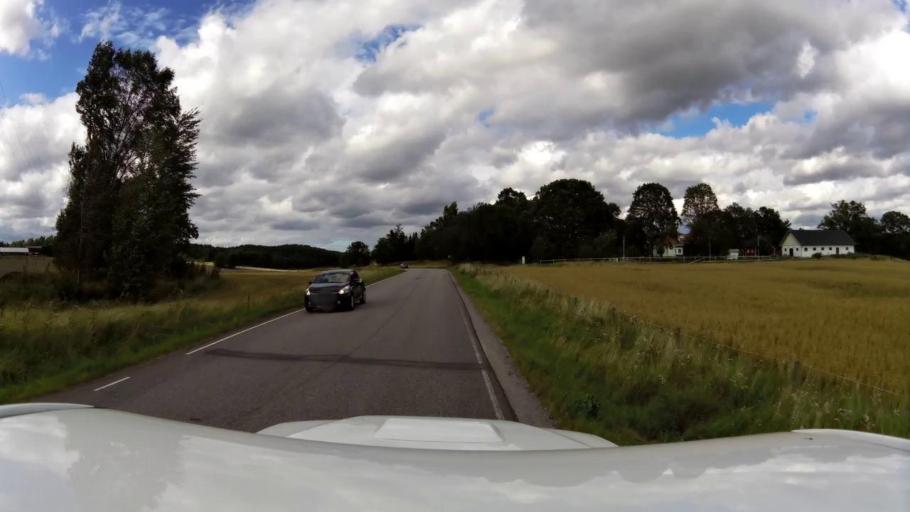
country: SE
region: OEstergoetland
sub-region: Linkopings Kommun
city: Sturefors
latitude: 58.3120
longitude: 15.7241
